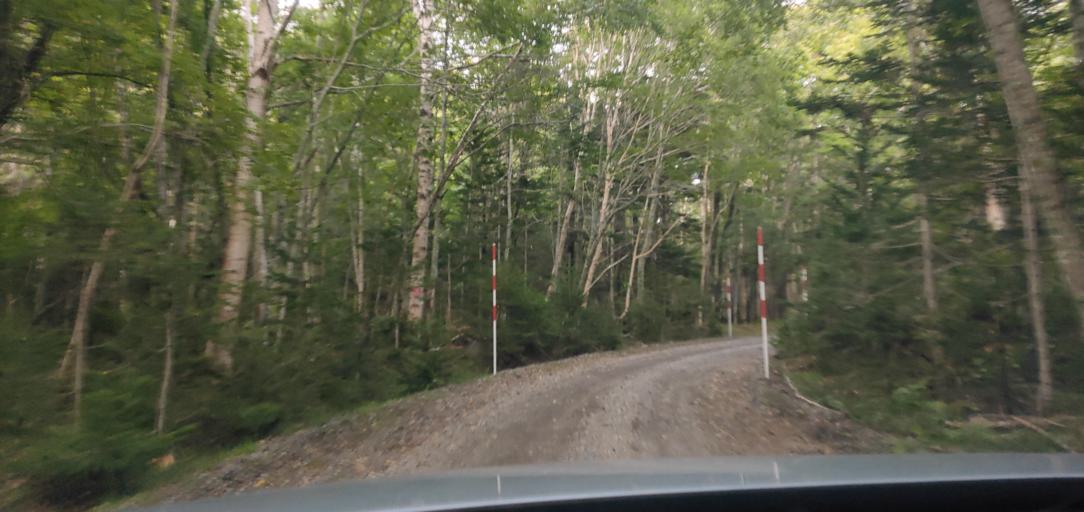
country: JP
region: Hokkaido
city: Kitami
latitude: 43.3779
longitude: 143.9689
